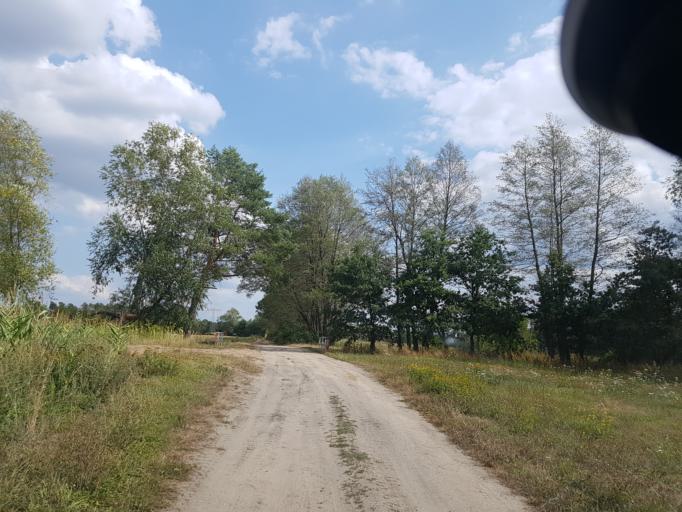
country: DE
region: Brandenburg
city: Calau
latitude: 51.7718
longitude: 13.9648
